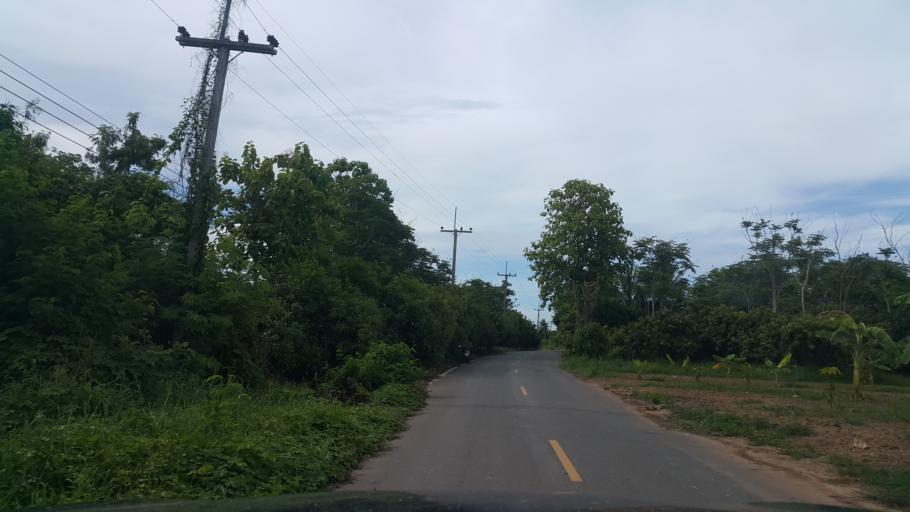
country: TH
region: Sukhothai
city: Si Nakhon
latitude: 17.2678
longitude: 99.9267
